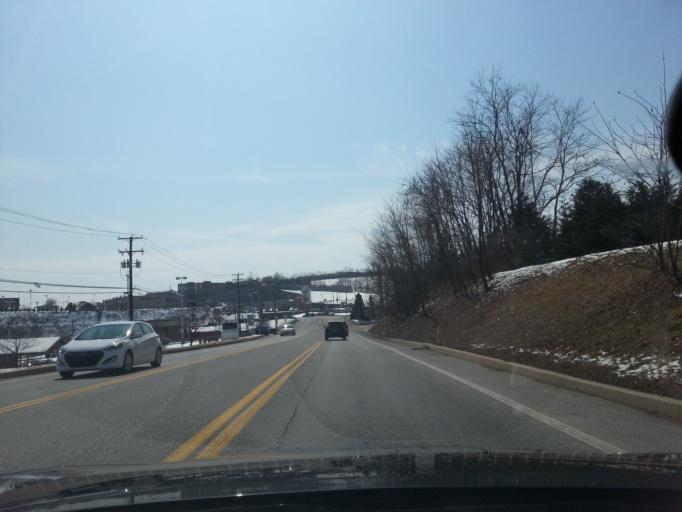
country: US
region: Pennsylvania
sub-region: York County
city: Shrewsbury
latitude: 39.7732
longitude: -76.6711
